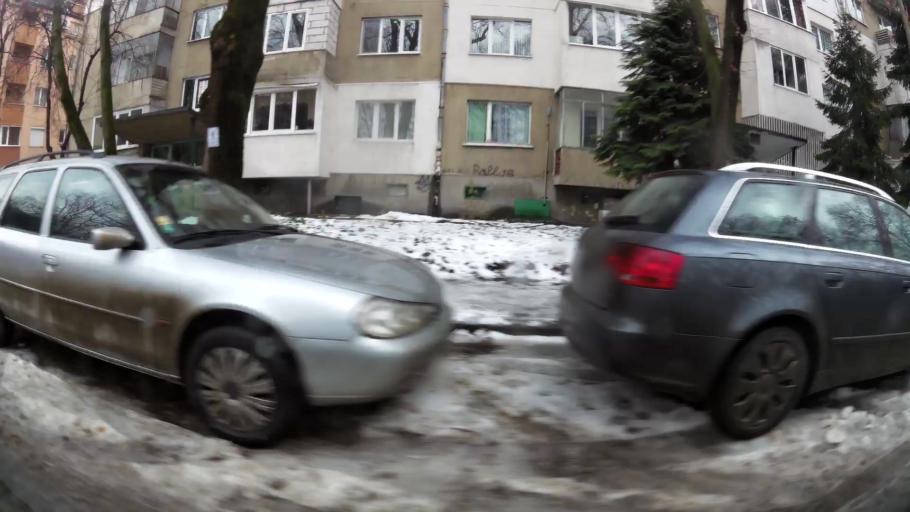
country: BG
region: Sofia-Capital
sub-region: Stolichna Obshtina
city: Sofia
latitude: 42.6695
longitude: 23.2828
